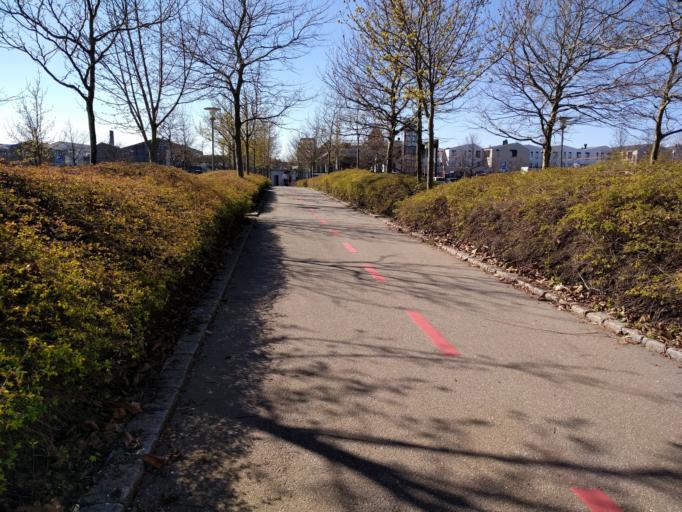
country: DK
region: Zealand
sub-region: Koge Kommune
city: Koge
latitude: 55.4572
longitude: 12.1889
